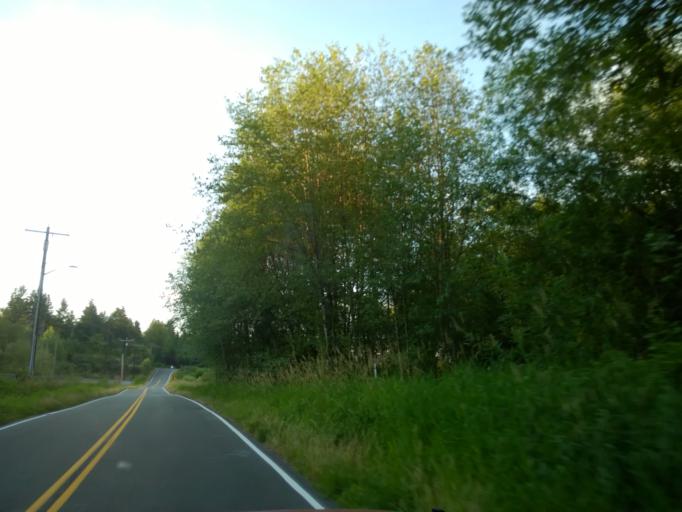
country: US
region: Washington
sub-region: King County
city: Woodinville
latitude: 47.7795
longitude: -122.1550
